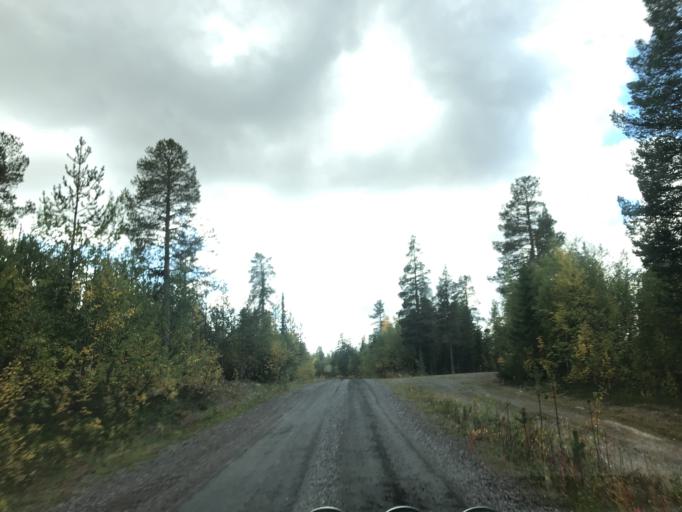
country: SE
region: Norrbotten
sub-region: Gallivare Kommun
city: Malmberget
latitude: 67.5933
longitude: 20.8815
